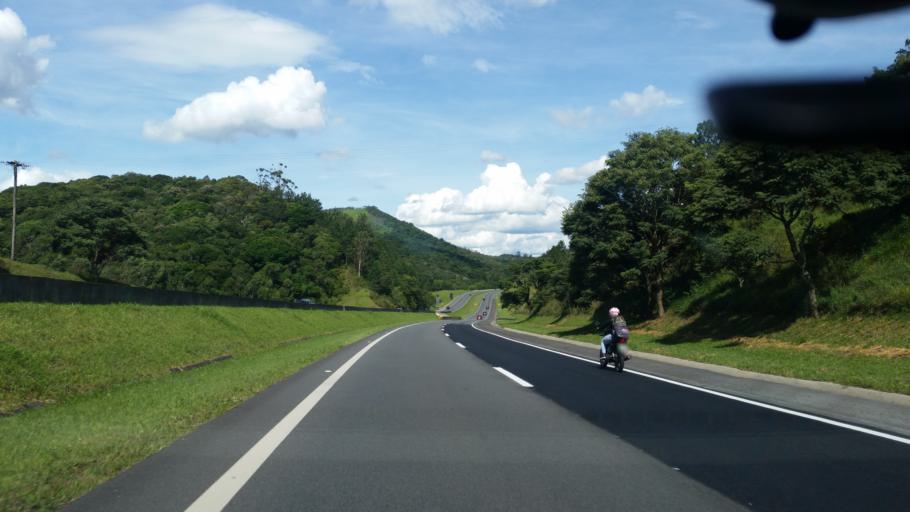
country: BR
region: Sao Paulo
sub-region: Piracaia
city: Piracaia
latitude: -23.1734
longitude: -46.2783
